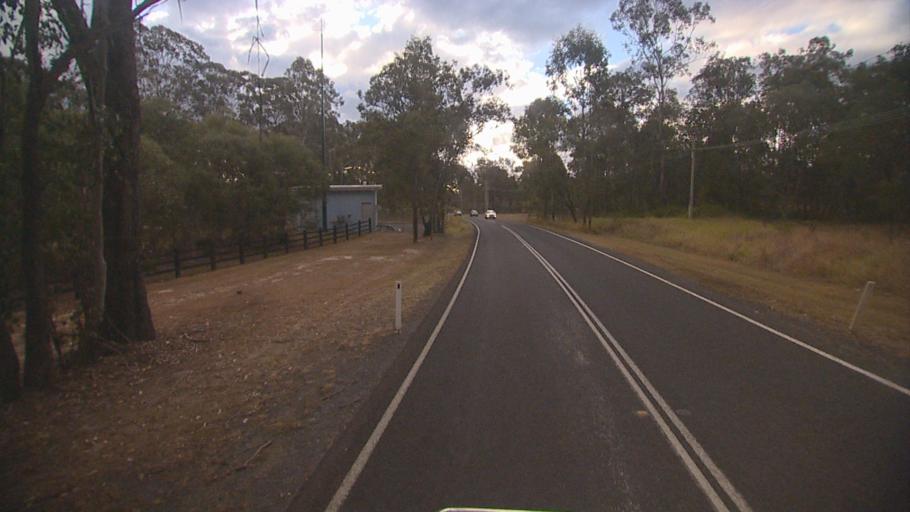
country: AU
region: Queensland
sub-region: Logan
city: Cedar Vale
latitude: -27.8633
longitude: 153.0580
